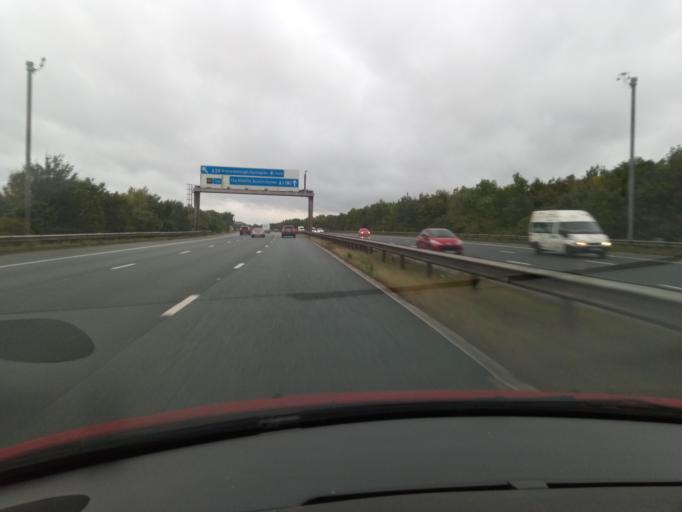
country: GB
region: England
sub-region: City and Borough of Leeds
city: Wetherby
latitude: 53.9982
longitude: -1.3662
